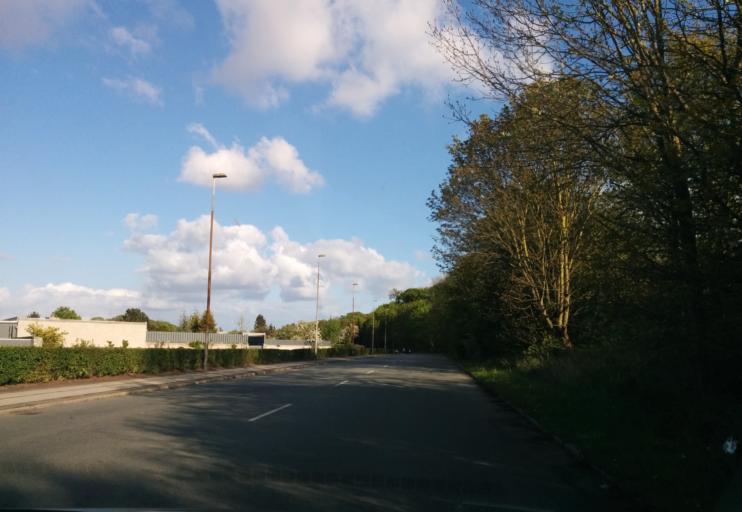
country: DK
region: Central Jutland
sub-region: Arhus Kommune
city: Stavtrup
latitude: 56.1213
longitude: 10.1361
